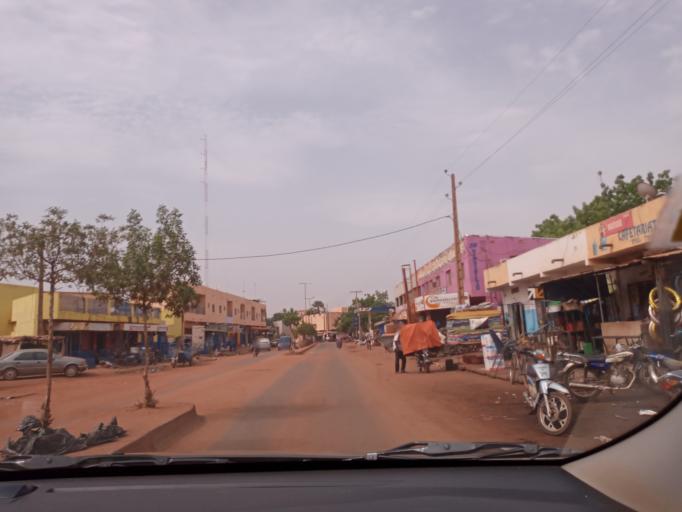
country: ML
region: Bamako
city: Bamako
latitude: 12.6788
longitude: -7.9239
